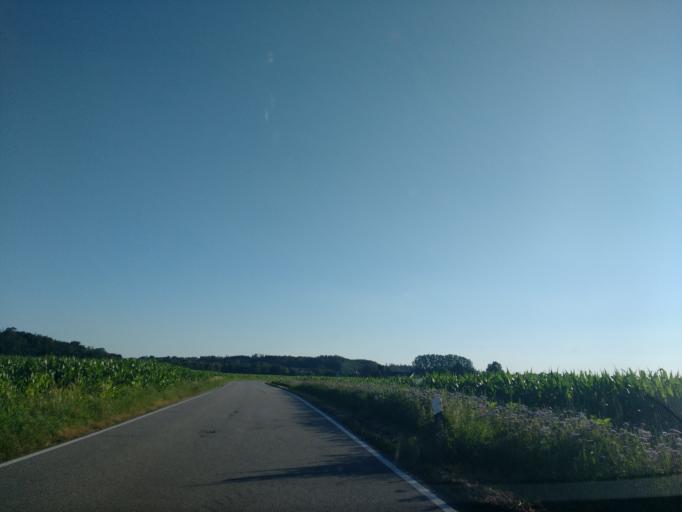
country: DE
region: Bavaria
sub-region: Upper Bavaria
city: Oberneukirchen
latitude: 48.2064
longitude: 12.4984
